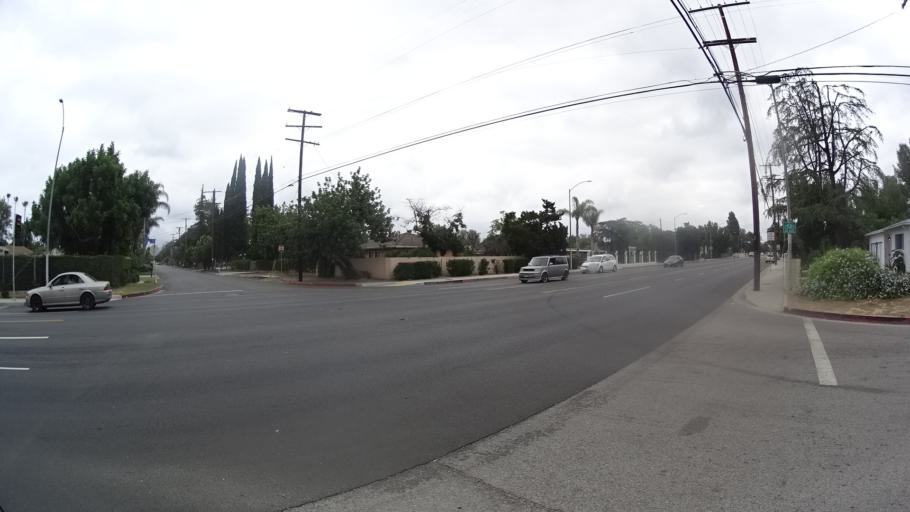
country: US
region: California
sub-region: Los Angeles County
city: San Fernando
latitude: 34.2427
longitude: -118.4634
